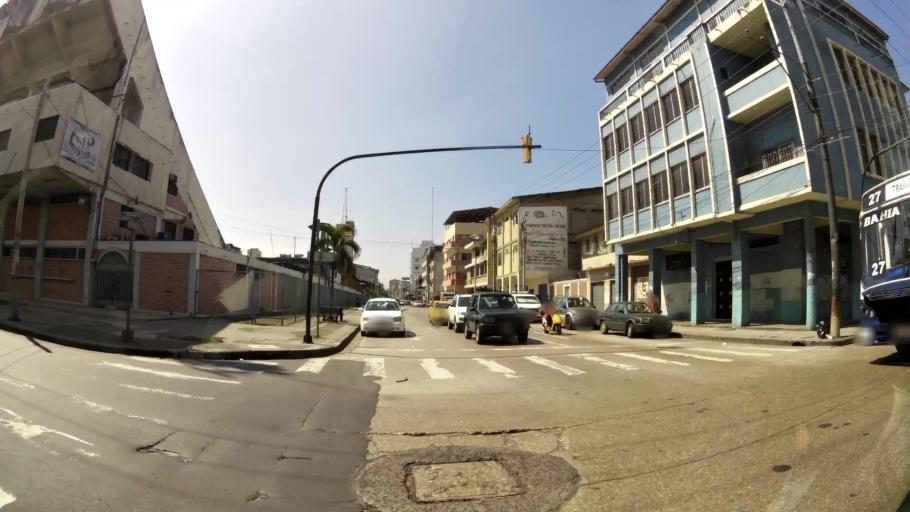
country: EC
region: Guayas
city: Guayaquil
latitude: -2.1905
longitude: -79.8933
